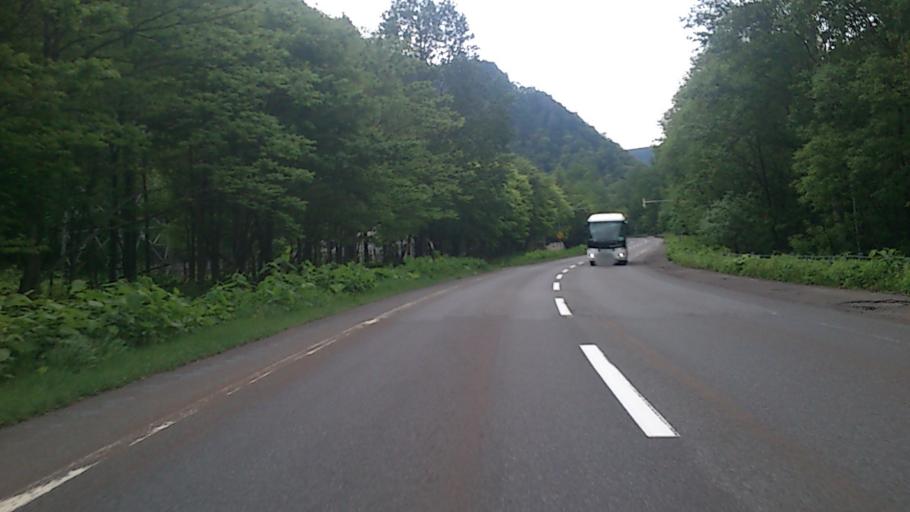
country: JP
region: Hokkaido
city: Kamikawa
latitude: 43.7524
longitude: 142.9308
